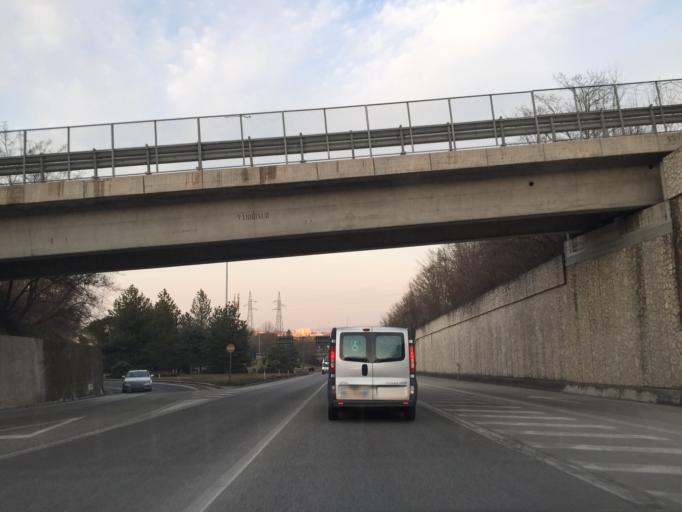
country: IT
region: Molise
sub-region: Provincia di Campobasso
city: Campobasso
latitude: 41.5524
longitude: 14.6463
